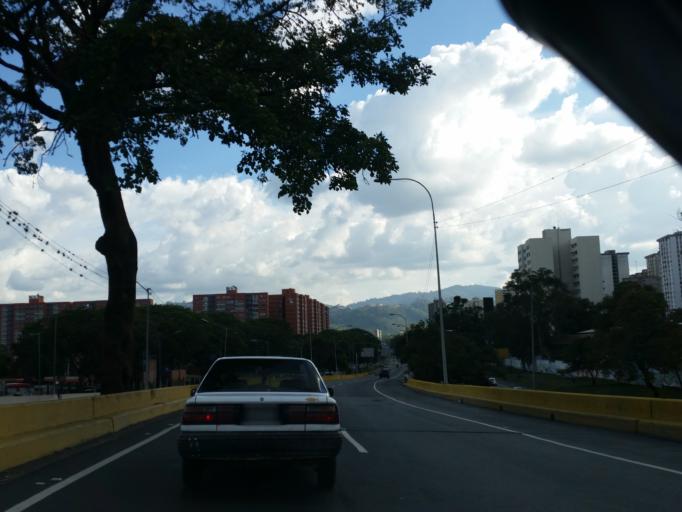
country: VE
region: Capital
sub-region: Municipio Libertador
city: Caracas
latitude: 10.4602
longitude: -66.9124
